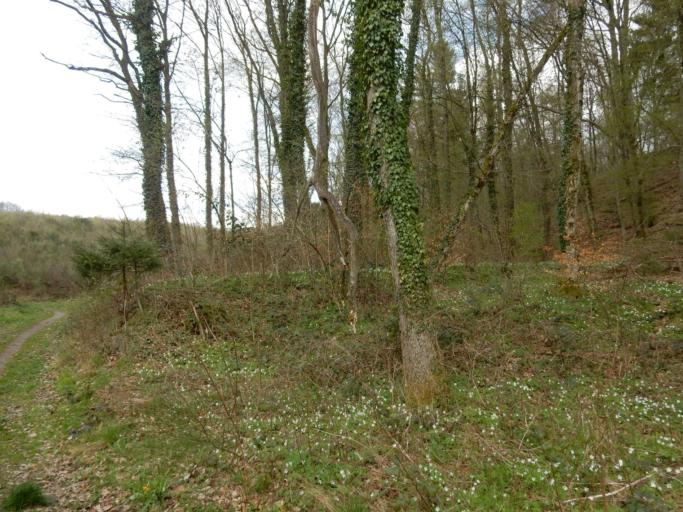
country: LU
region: Luxembourg
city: Eischen
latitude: 49.6733
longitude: 5.8826
